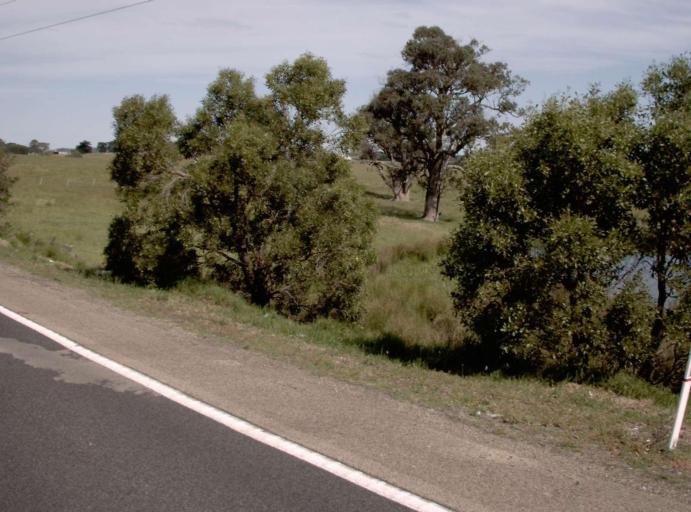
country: AU
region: Victoria
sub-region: East Gippsland
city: Lakes Entrance
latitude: -37.8215
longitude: 147.8423
